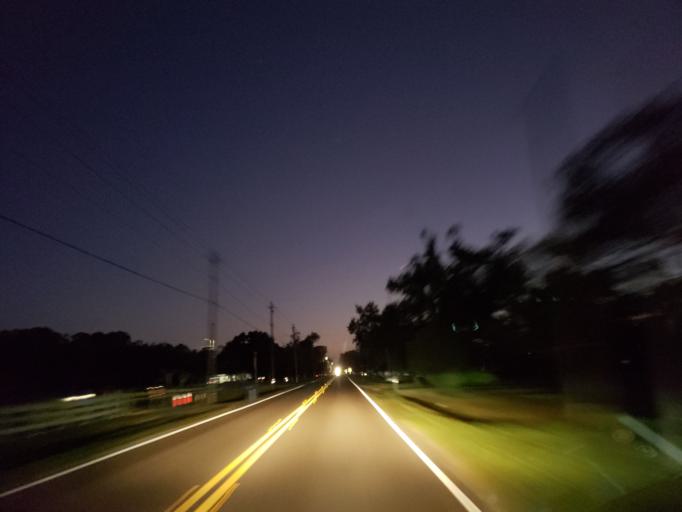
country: US
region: Florida
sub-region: Hillsborough County
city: Dover
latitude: 27.9852
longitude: -82.2198
